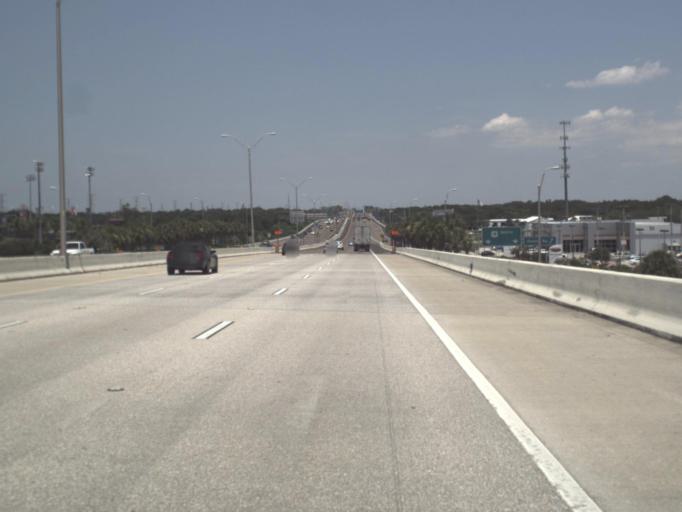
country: US
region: Florida
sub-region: Pinellas County
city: Safety Harbor
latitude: 27.9686
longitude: -82.7297
